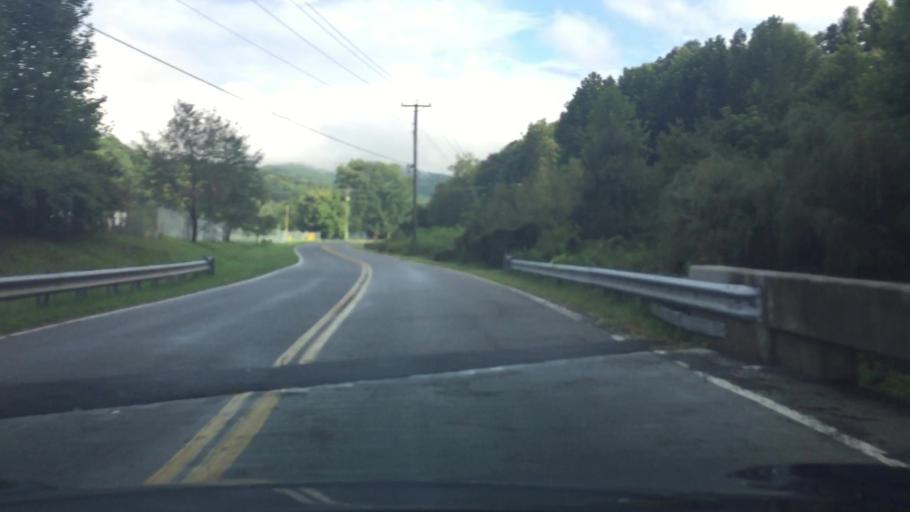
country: US
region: Virginia
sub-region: Smyth County
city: Atkins
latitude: 36.8580
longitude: -81.4314
